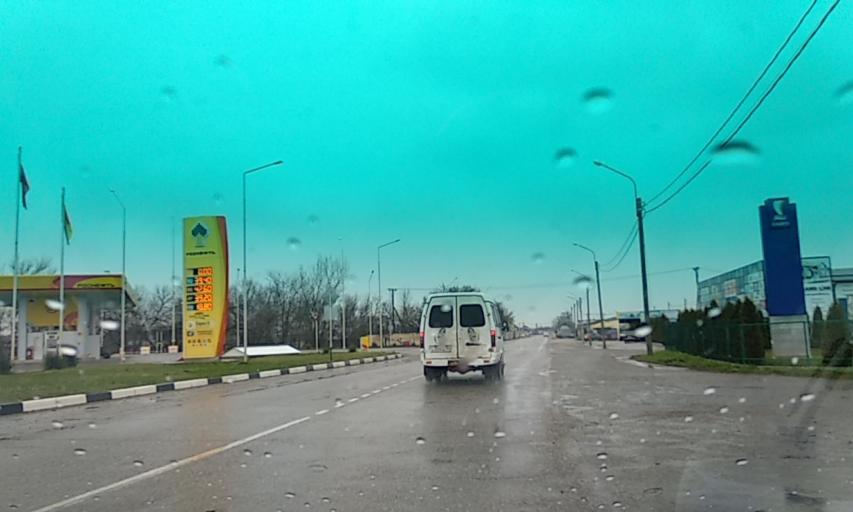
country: RU
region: Krasnodarskiy
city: Belorechensk
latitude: 44.7946
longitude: 39.8624
